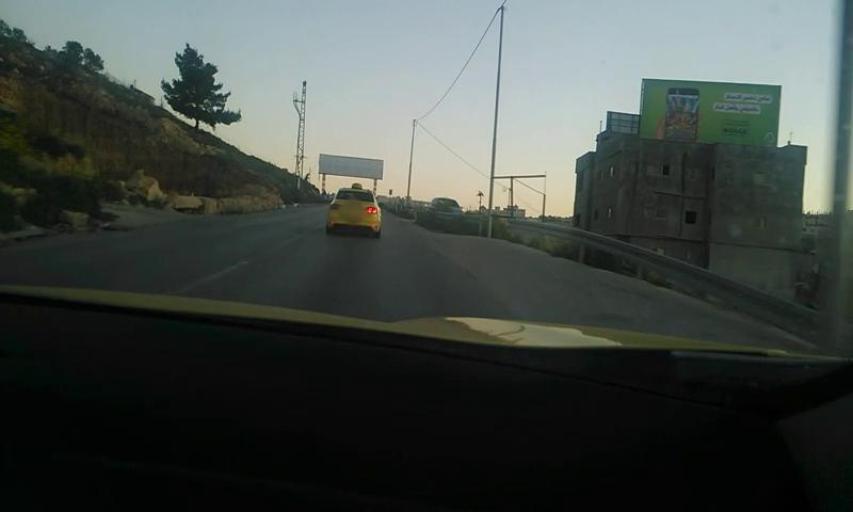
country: PS
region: West Bank
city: Jifna
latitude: 31.9515
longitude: 35.2149
